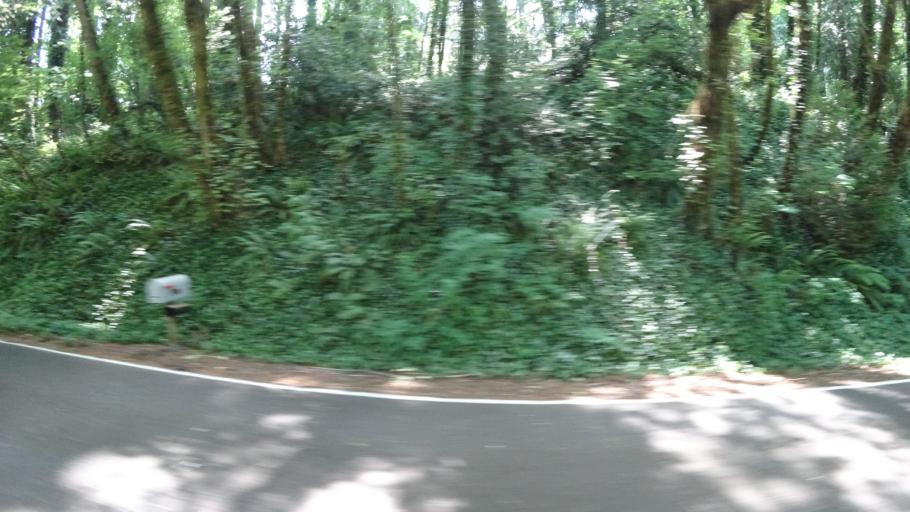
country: US
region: Oregon
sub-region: Clackamas County
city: Lake Oswego
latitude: 45.4419
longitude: -122.6957
